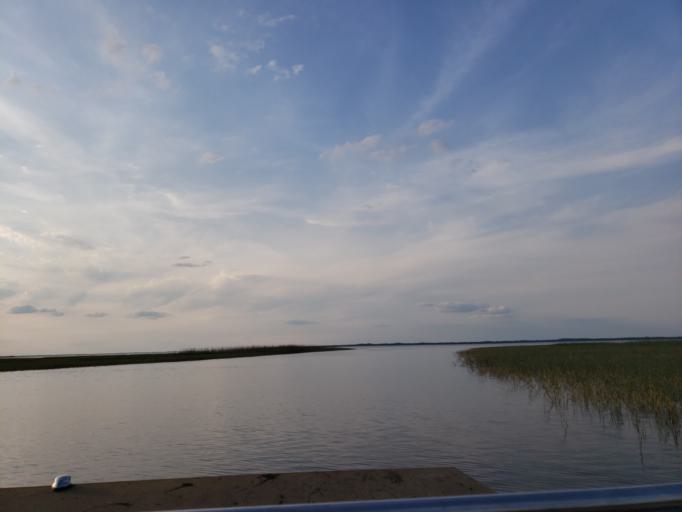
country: US
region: Florida
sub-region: Osceola County
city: Poinciana
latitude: 28.1414
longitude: -81.3516
